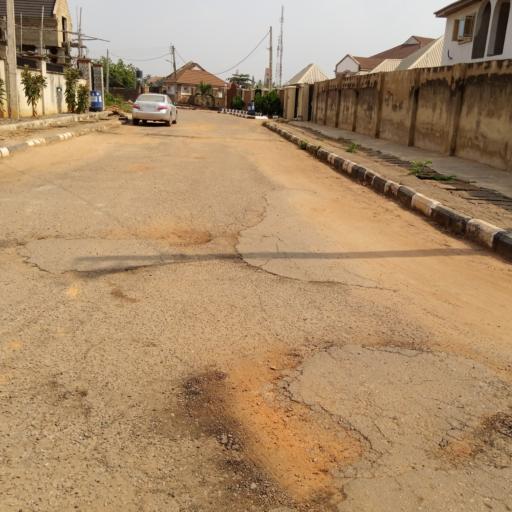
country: NG
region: Oyo
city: Ibadan
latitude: 7.4285
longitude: 3.9083
